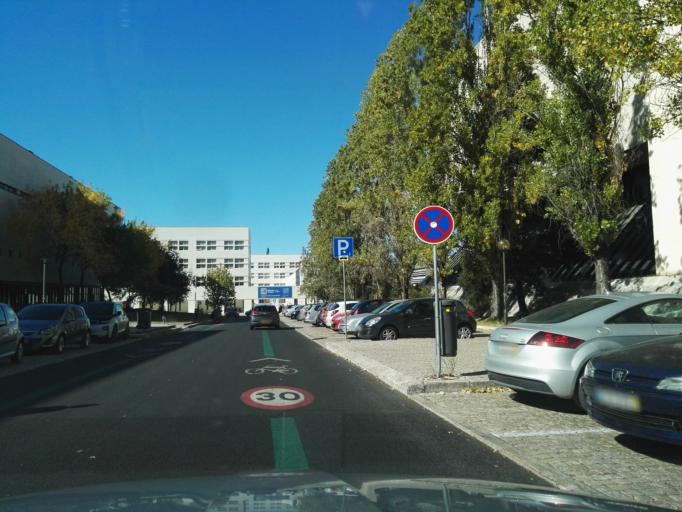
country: PT
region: Lisbon
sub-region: Odivelas
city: Olival do Basto
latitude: 38.7543
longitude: -9.1570
